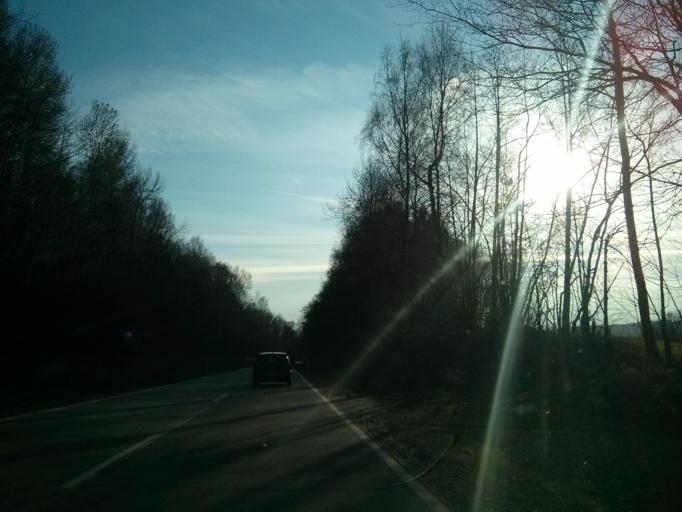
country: DE
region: Bavaria
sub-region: Lower Bavaria
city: Deggendorf
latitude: 48.8429
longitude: 12.9886
